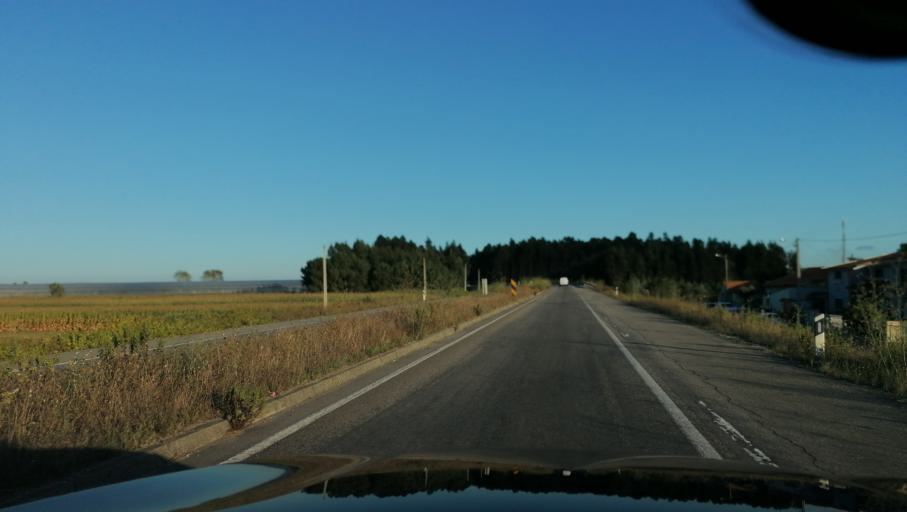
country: PT
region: Aveiro
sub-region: Aveiro
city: Oliveirinha
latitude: 40.5999
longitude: -8.6168
